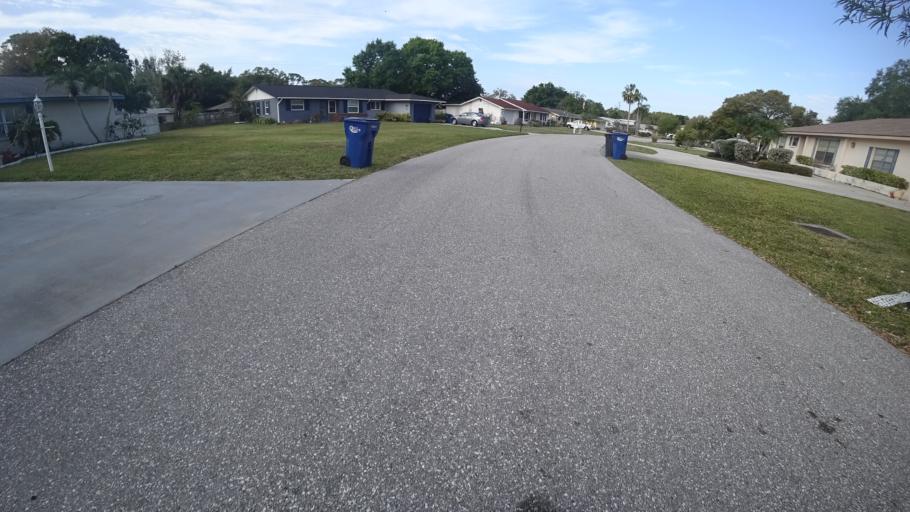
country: US
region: Florida
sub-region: Manatee County
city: Whitfield
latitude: 27.4214
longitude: -82.5527
